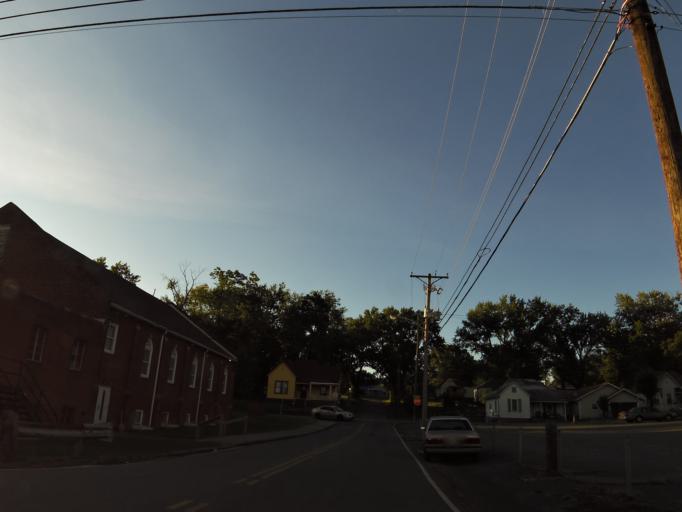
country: US
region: Tennessee
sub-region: Knox County
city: Knoxville
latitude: 35.9738
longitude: -83.9452
